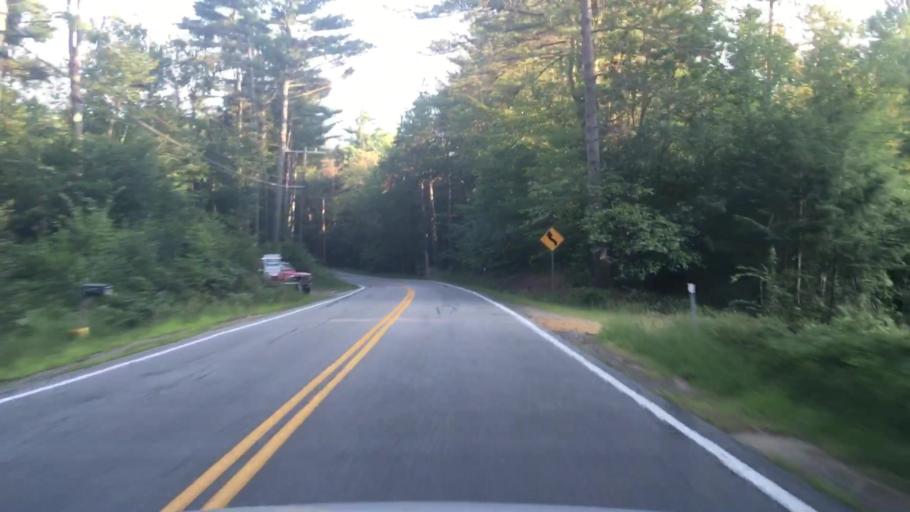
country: US
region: New Hampshire
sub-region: Belknap County
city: Laconia
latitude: 43.4871
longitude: -71.4340
